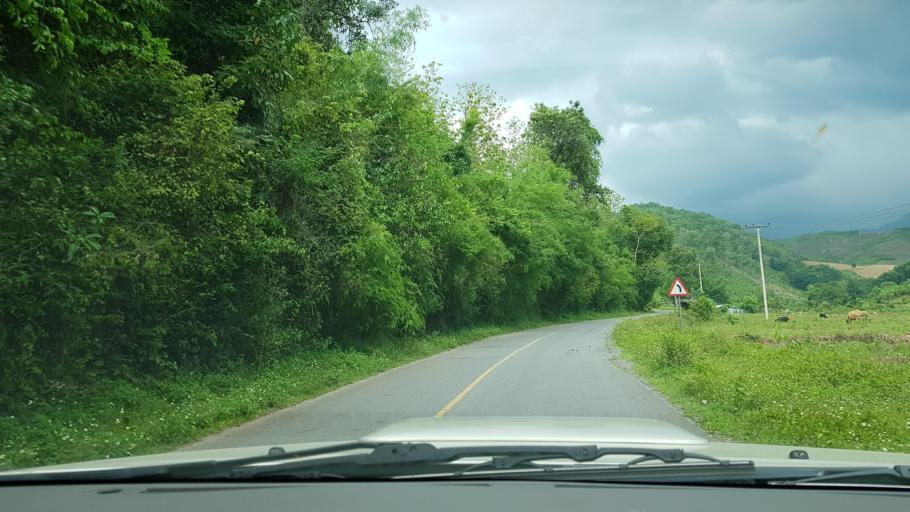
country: LA
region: Loungnamtha
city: Muang Nale
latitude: 20.3572
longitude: 101.7028
